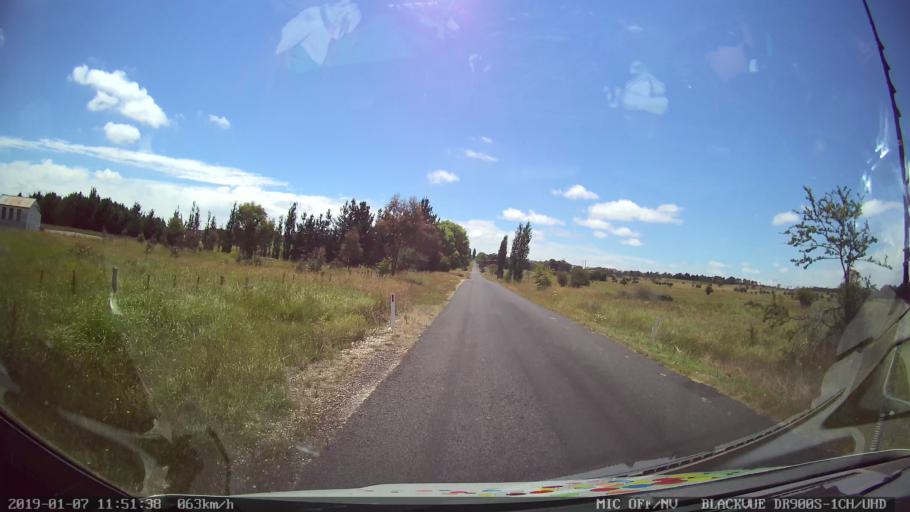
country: AU
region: New South Wales
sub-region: Guyra
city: Guyra
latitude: -30.3075
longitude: 151.6470
